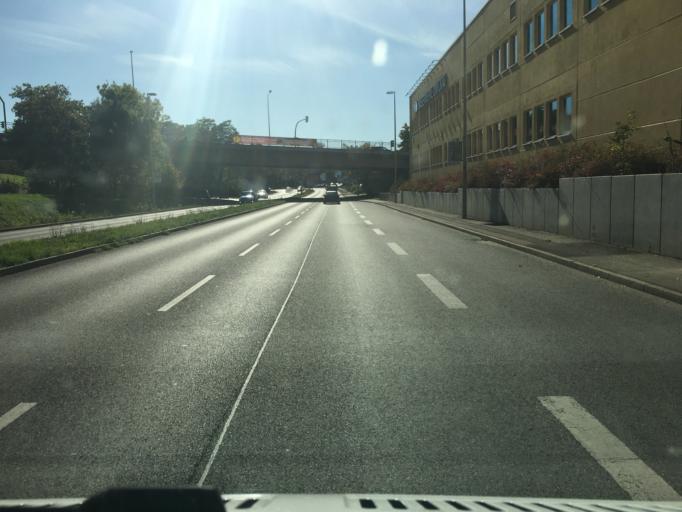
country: DE
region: Saxony
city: Zwickau
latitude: 50.7158
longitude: 12.5004
